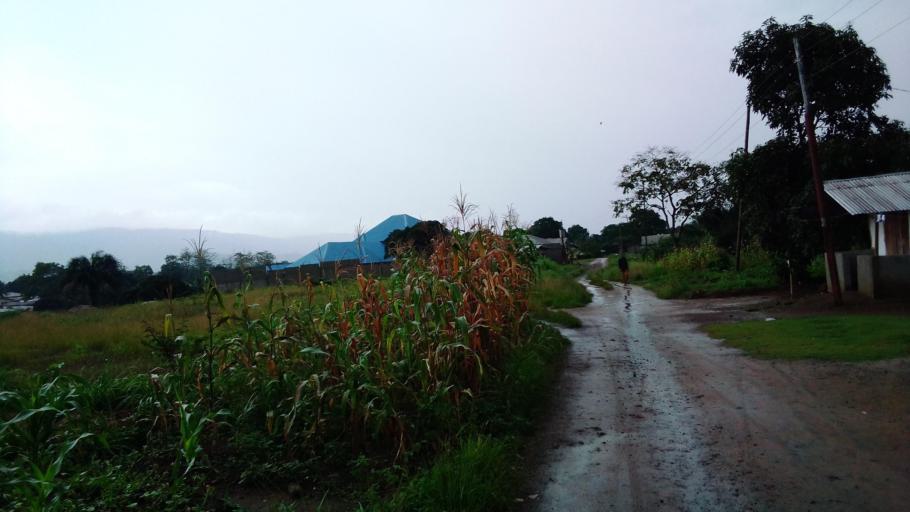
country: SL
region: Eastern Province
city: Kenema
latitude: 7.8807
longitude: -11.1736
